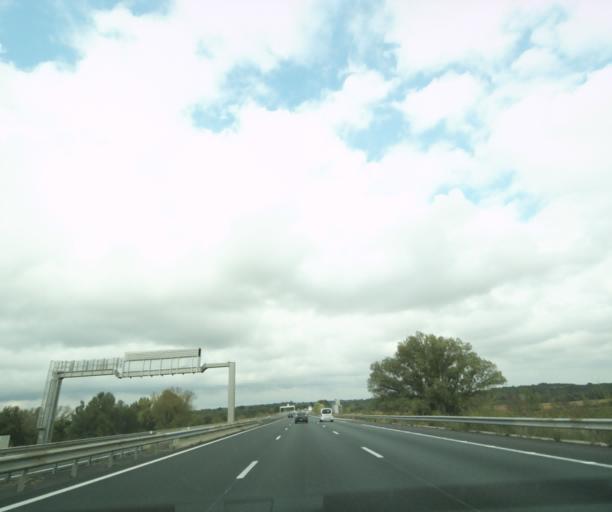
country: FR
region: Languedoc-Roussillon
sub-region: Departement de l'Herault
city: Cers
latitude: 43.3520
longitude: 3.3343
